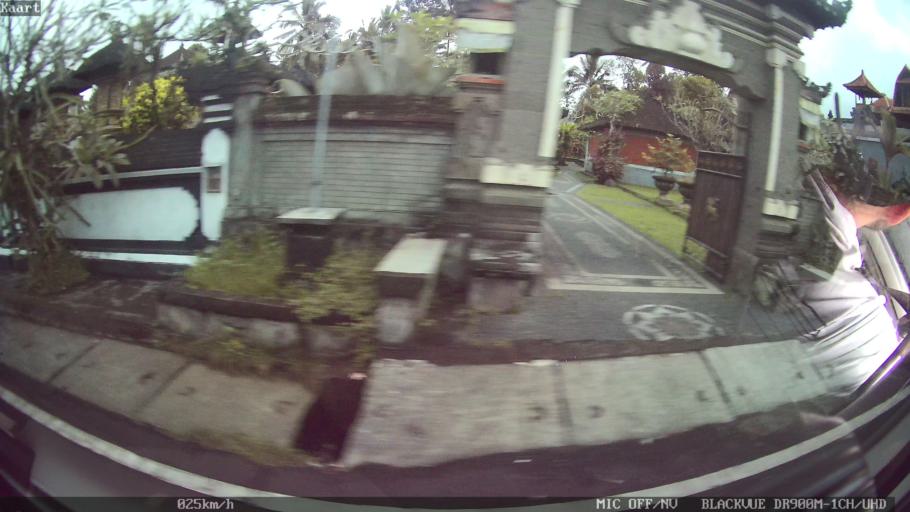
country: ID
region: Bali
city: Pemijian
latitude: -8.4462
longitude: 115.2271
